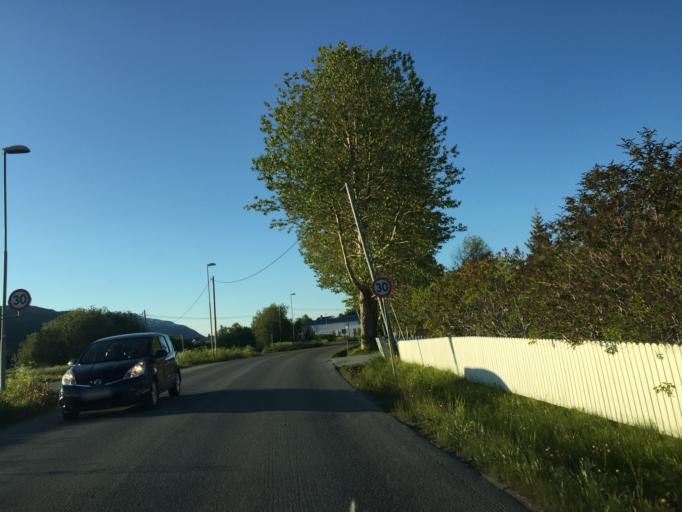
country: NO
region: Nordland
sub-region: Bodo
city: Loding
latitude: 67.2971
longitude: 14.7293
